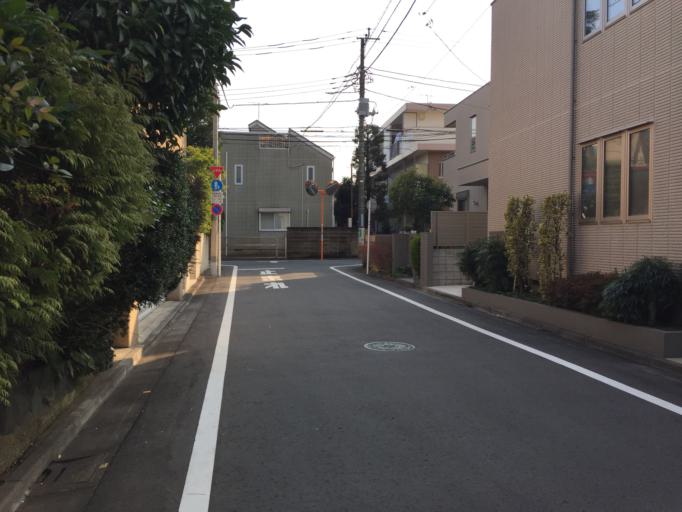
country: JP
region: Tokyo
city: Tokyo
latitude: 35.6563
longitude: 139.6445
